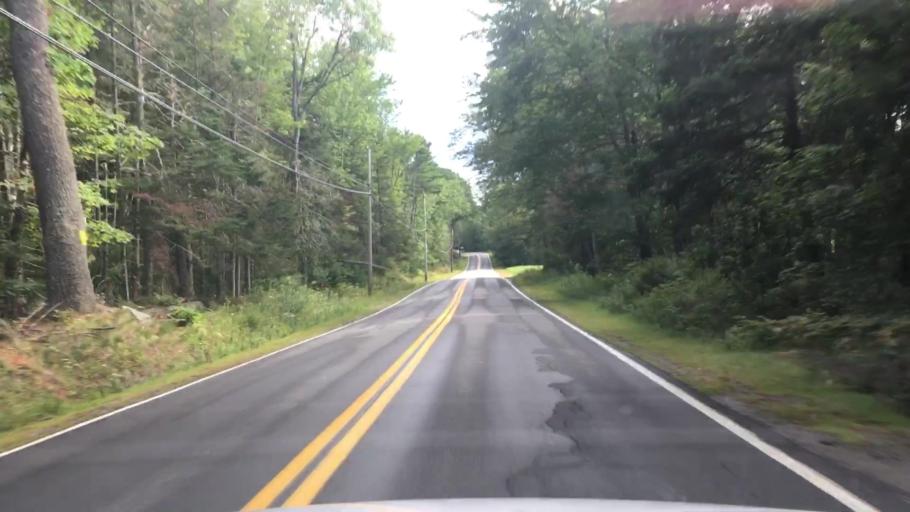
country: US
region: Maine
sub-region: Hancock County
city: Ellsworth
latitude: 44.4796
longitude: -68.4207
